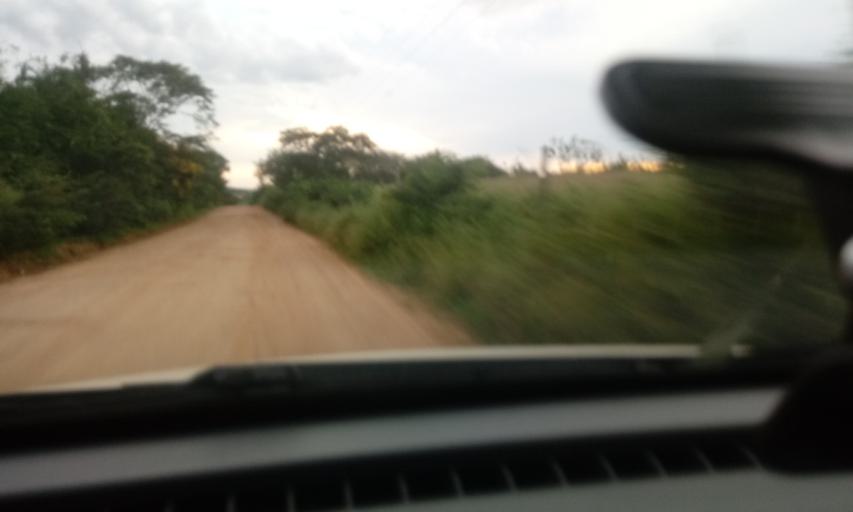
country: BR
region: Bahia
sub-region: Riacho De Santana
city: Riacho de Santana
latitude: -13.7943
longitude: -42.7322
